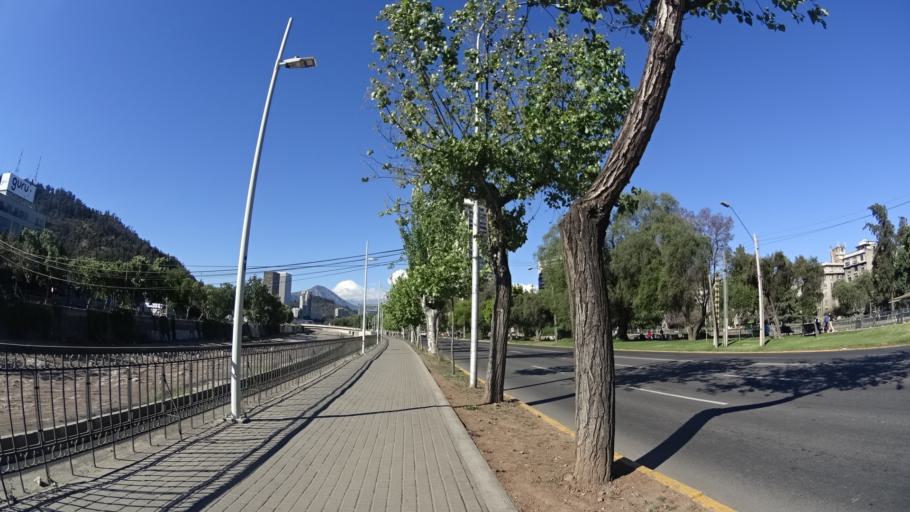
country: CL
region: Santiago Metropolitan
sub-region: Provincia de Santiago
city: Santiago
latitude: -33.4314
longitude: -70.6255
